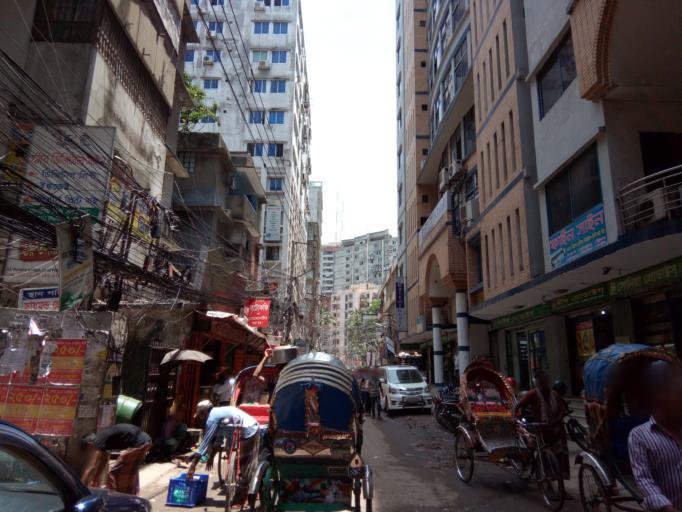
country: BD
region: Dhaka
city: Paltan
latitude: 23.7308
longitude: 90.4117
